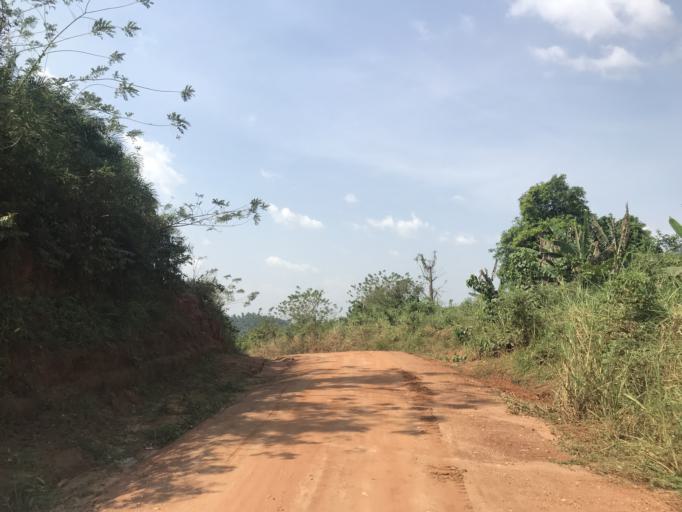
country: NG
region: Osun
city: Ilesa
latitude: 7.6257
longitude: 4.6933
